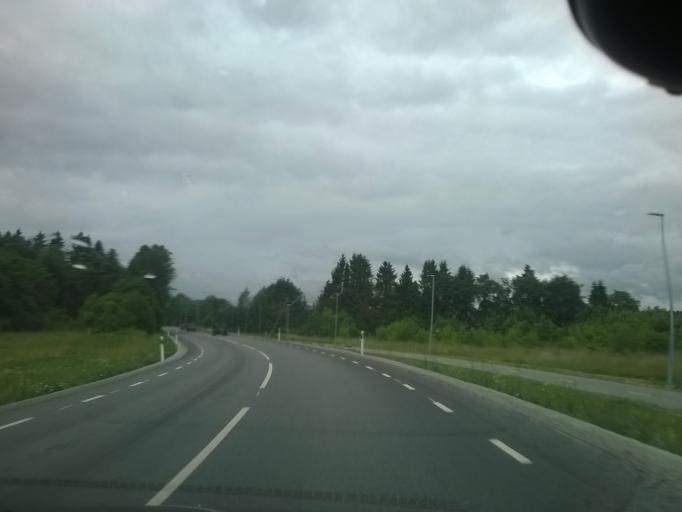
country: EE
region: Harju
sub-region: Rae vald
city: Jueri
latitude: 59.3677
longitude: 24.8701
